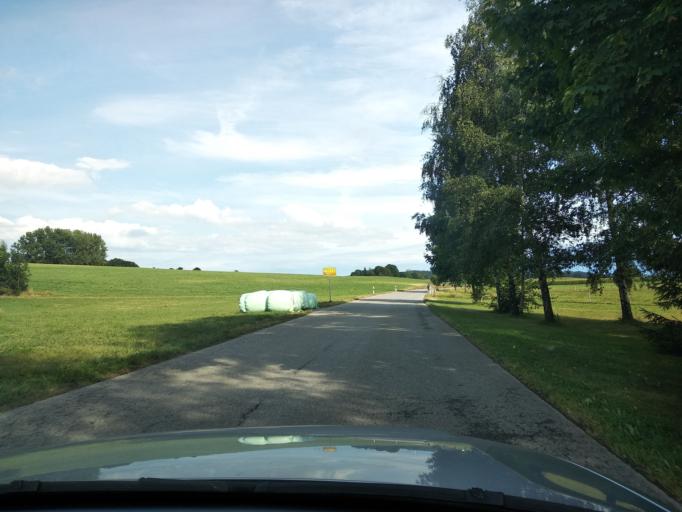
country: DE
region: Bavaria
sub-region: Swabia
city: Dietmannsried
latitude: 47.8232
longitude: 10.3117
